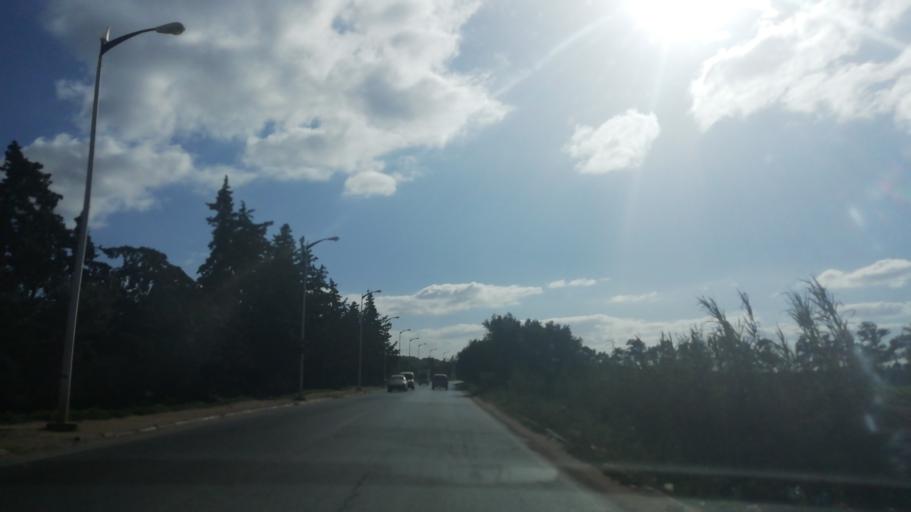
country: DZ
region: Mostaganem
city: Mostaganem
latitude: 35.9903
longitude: 0.2923
